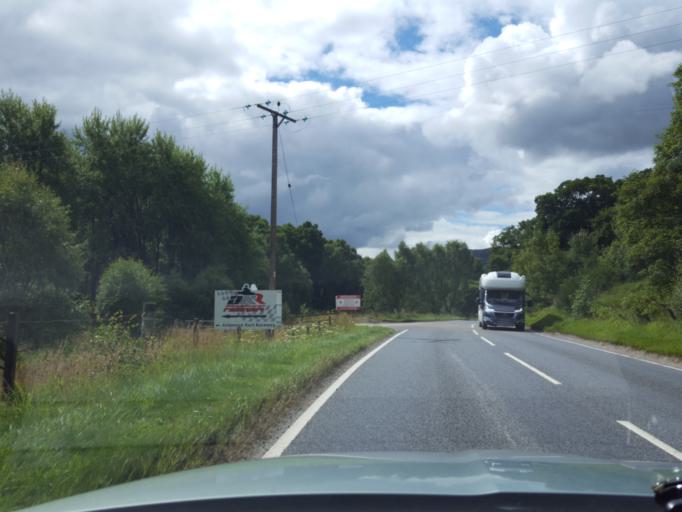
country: GB
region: Scotland
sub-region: Highland
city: Aviemore
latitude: 57.2121
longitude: -3.8219
